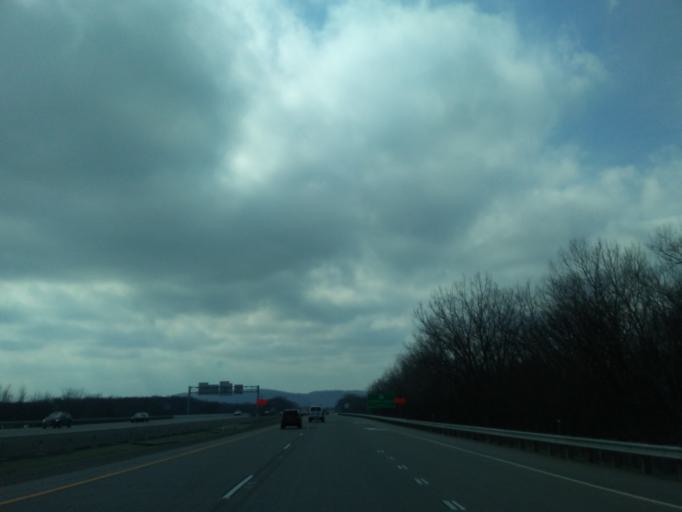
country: US
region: Wisconsin
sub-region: La Crosse County
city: North La Crosse
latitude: 43.8638
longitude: -91.2409
